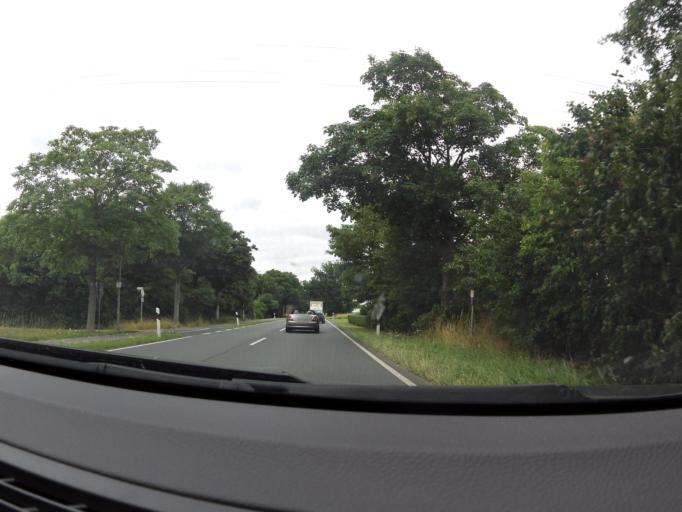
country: DE
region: North Rhine-Westphalia
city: Straelen
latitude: 51.4573
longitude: 6.2754
